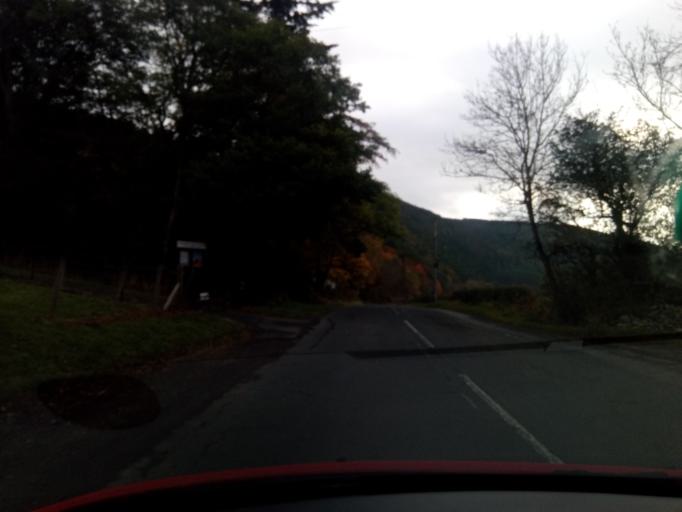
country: GB
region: Scotland
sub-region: The Scottish Borders
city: Selkirk
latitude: 55.6032
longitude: -2.8738
